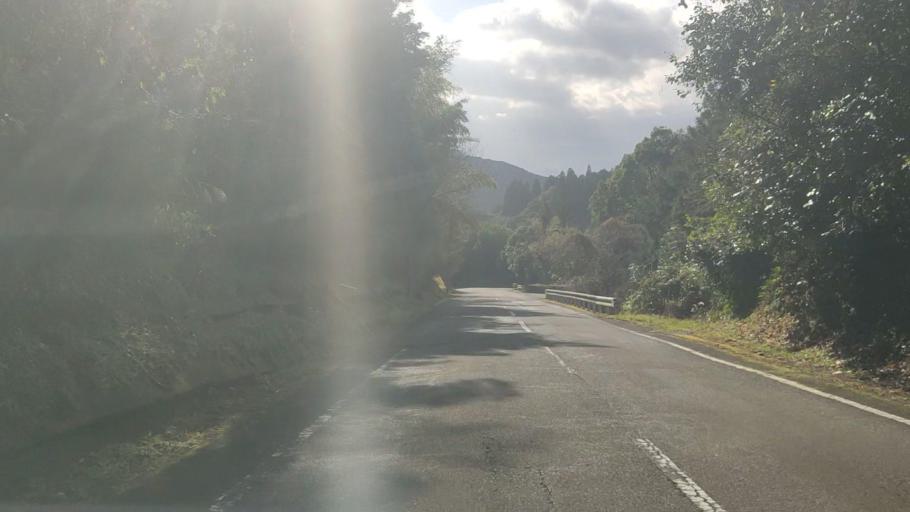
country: JP
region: Kumamoto
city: Hitoyoshi
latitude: 32.3182
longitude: 130.8436
